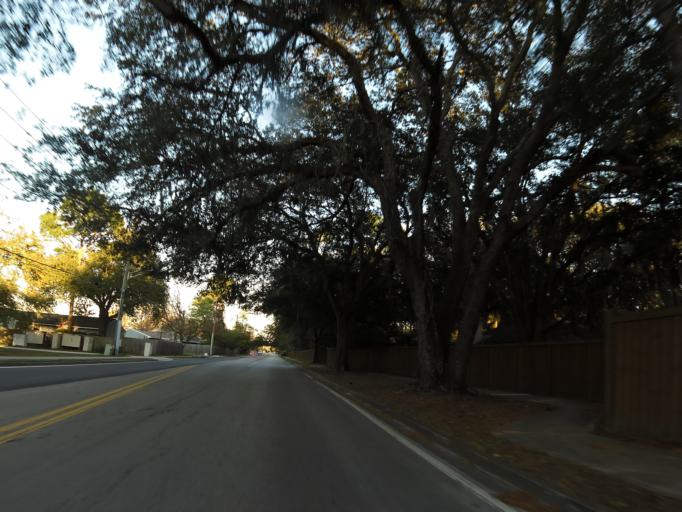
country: US
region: Florida
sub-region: Saint Johns County
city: Fruit Cove
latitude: 30.1722
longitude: -81.5844
